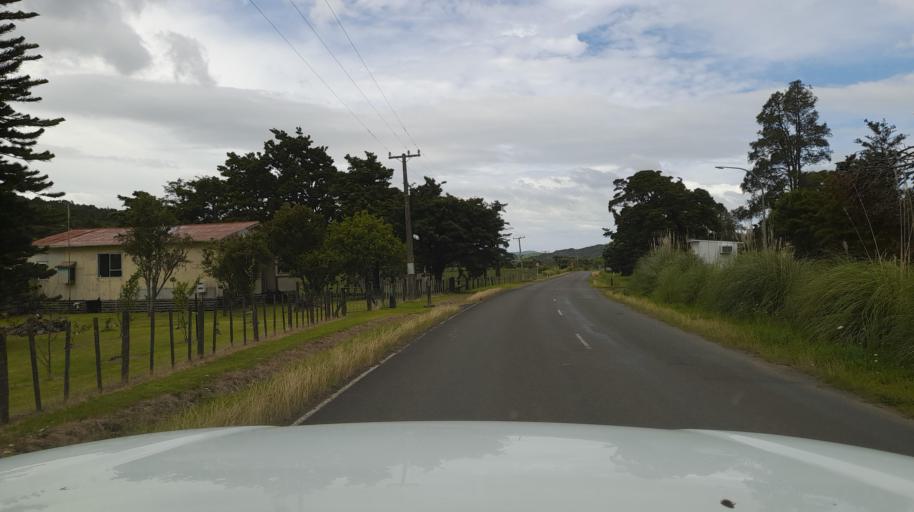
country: NZ
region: Northland
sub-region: Far North District
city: Kaitaia
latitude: -35.3823
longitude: 173.3841
